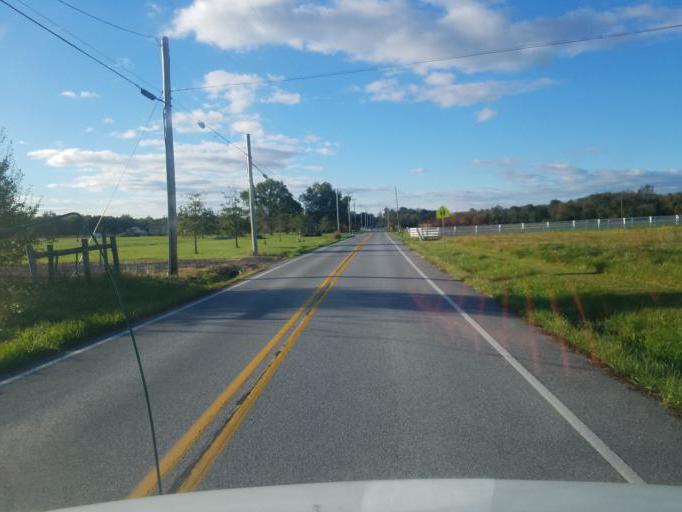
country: US
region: Pennsylvania
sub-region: Adams County
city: Gettysburg
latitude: 39.8606
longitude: -77.2280
